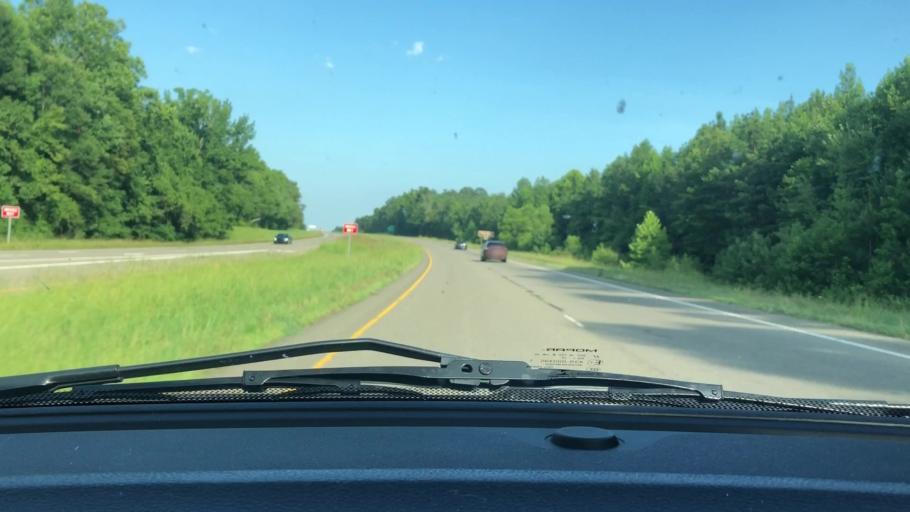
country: US
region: North Carolina
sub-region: Chatham County
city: Farmville
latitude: 35.6107
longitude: -79.3413
